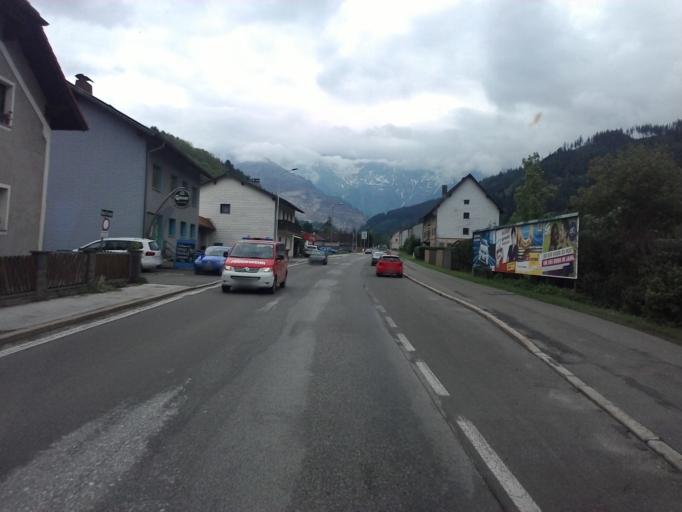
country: AT
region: Styria
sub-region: Politischer Bezirk Leoben
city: Eisenerz
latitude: 47.5567
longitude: 14.8700
